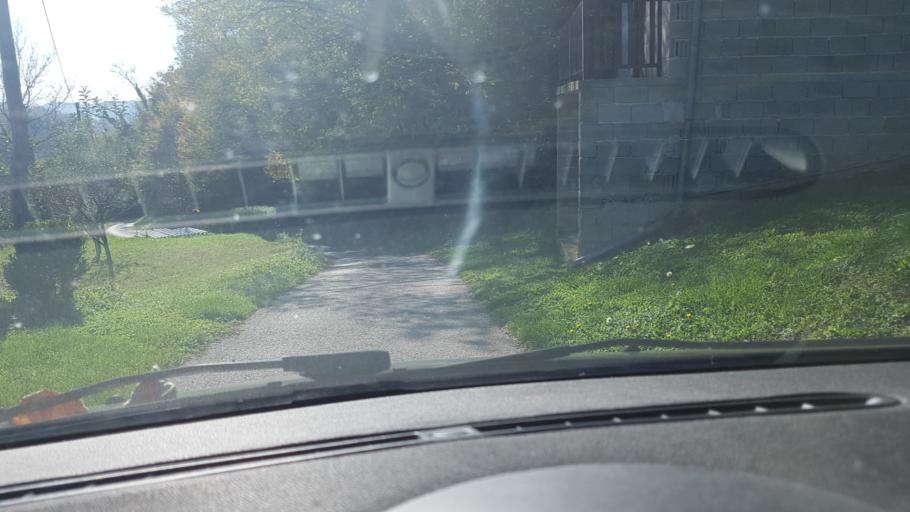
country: HR
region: Krapinsko-Zagorska
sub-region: Grad Krapina
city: Krapina
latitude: 46.1567
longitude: 15.8813
